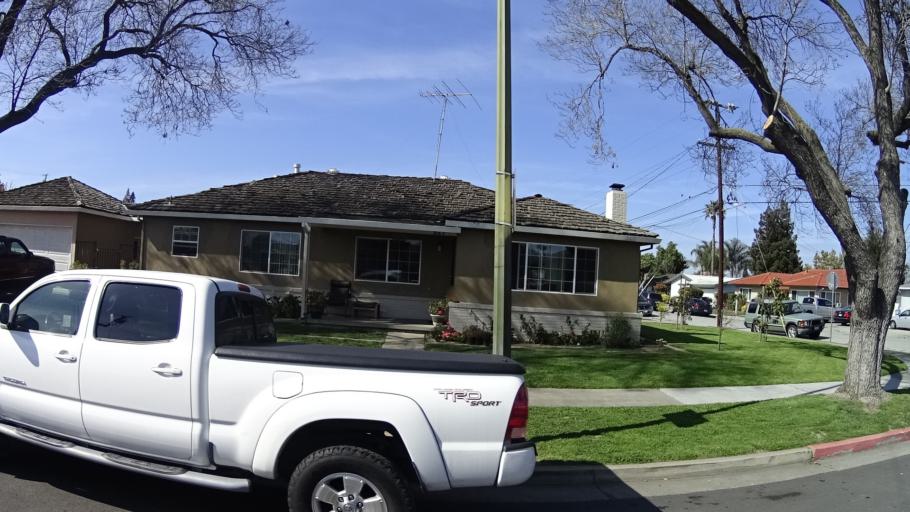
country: US
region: California
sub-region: Santa Clara County
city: San Jose
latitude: 37.3580
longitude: -121.8814
